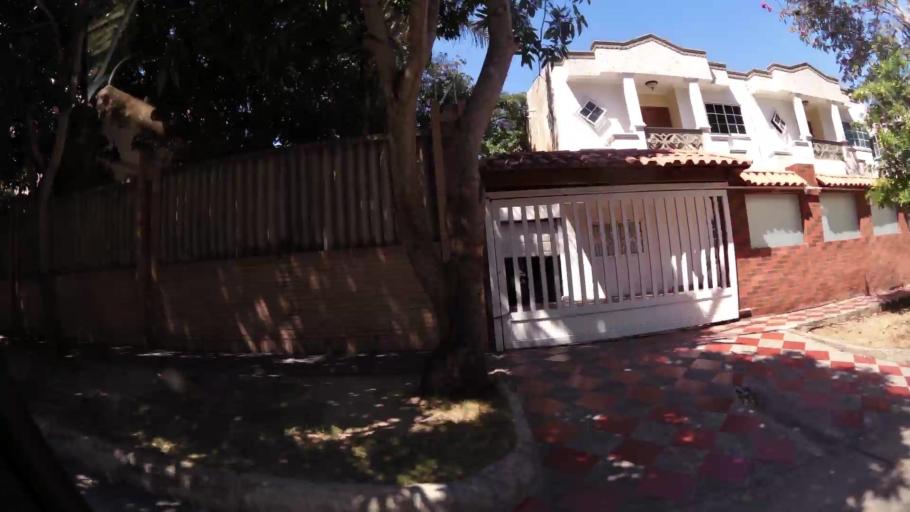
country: CO
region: Atlantico
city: Barranquilla
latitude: 11.0107
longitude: -74.8084
